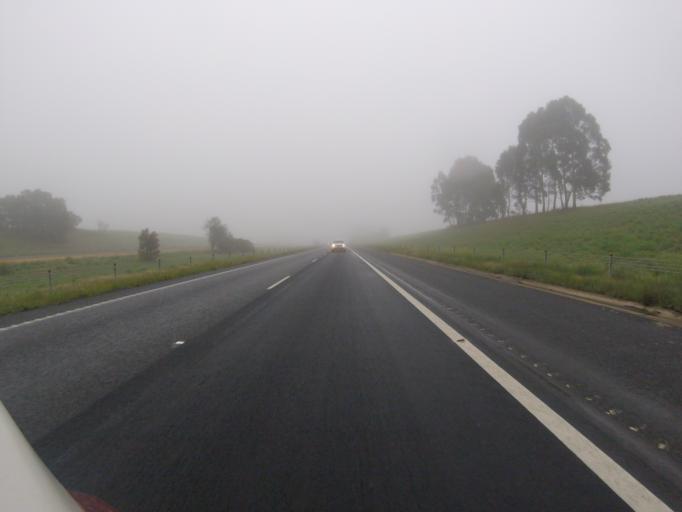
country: AU
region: Victoria
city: Brown Hill
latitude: -37.5509
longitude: 144.0677
